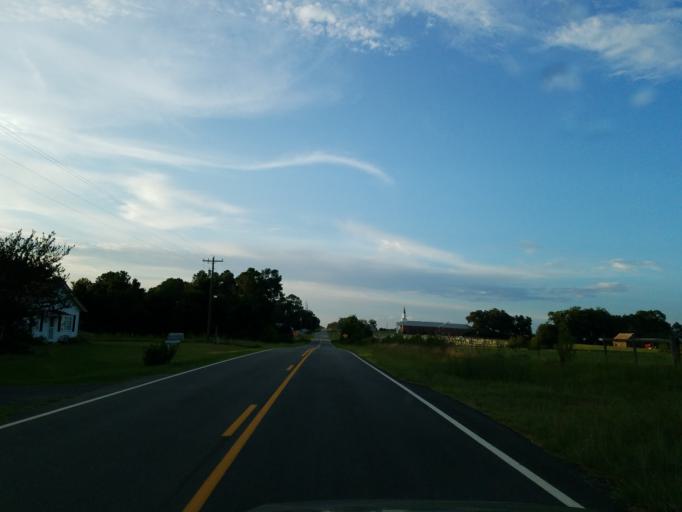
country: US
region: Georgia
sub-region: Turner County
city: Ashburn
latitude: 31.6549
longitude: -83.5663
